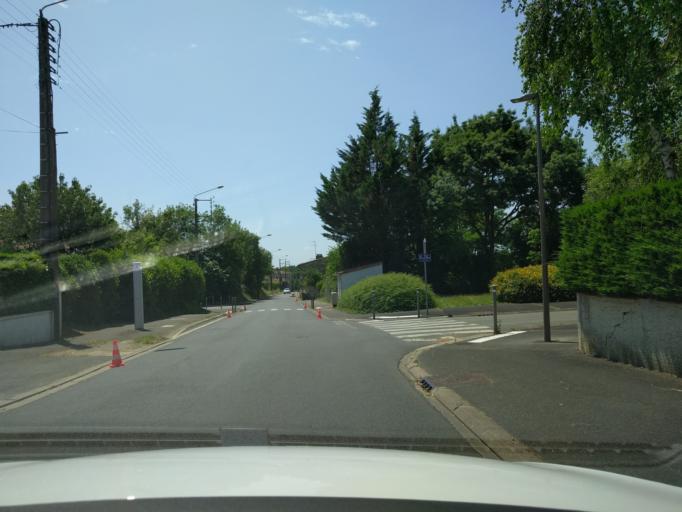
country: FR
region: Poitou-Charentes
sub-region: Departement des Deux-Sevres
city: Niort
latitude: 46.3431
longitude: -0.4634
